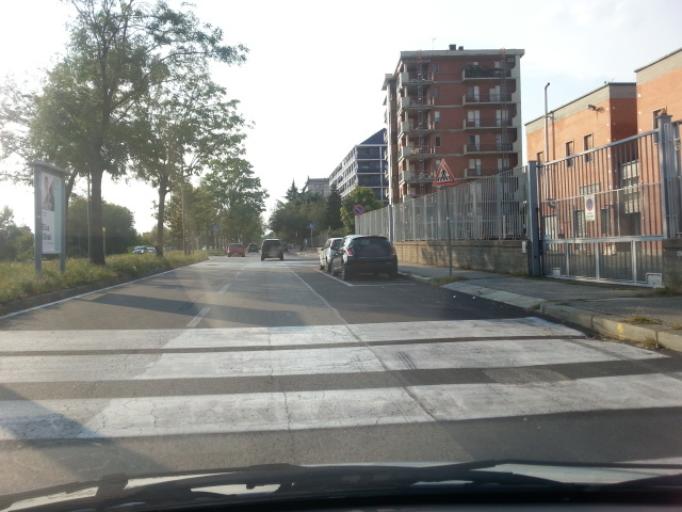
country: IT
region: Piedmont
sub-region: Provincia di Torino
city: Fornaci
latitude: 45.0162
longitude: 7.6128
